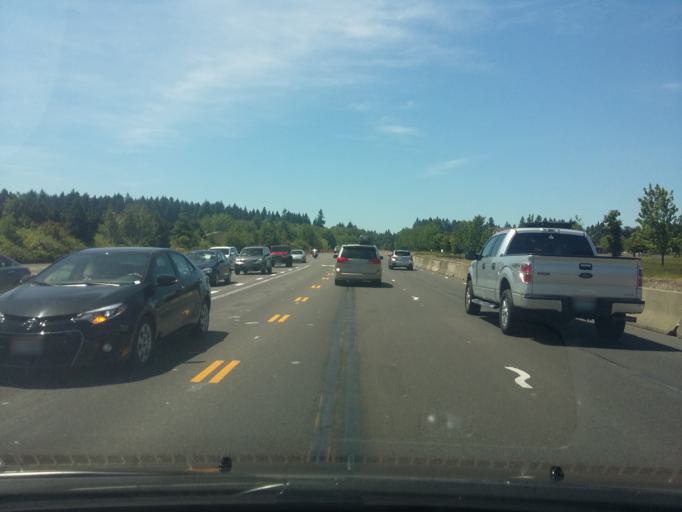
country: US
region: Washington
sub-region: Clark County
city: Five Corners
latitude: 45.6824
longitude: -122.5764
